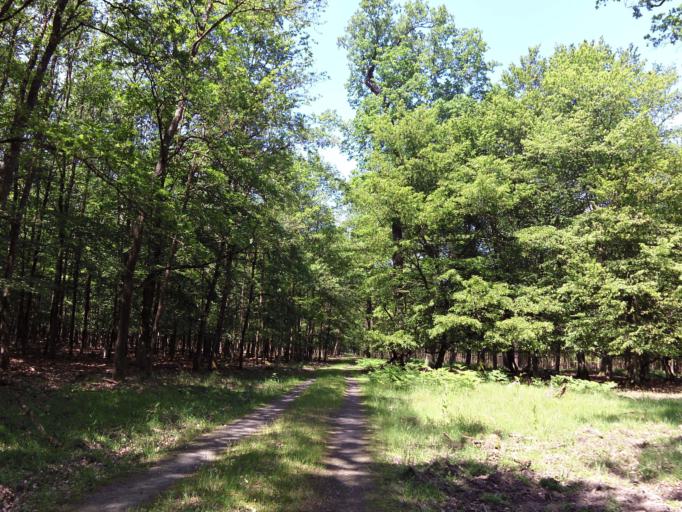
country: DE
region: Hesse
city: Morfelden-Walldorf
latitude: 50.0056
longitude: 8.5361
